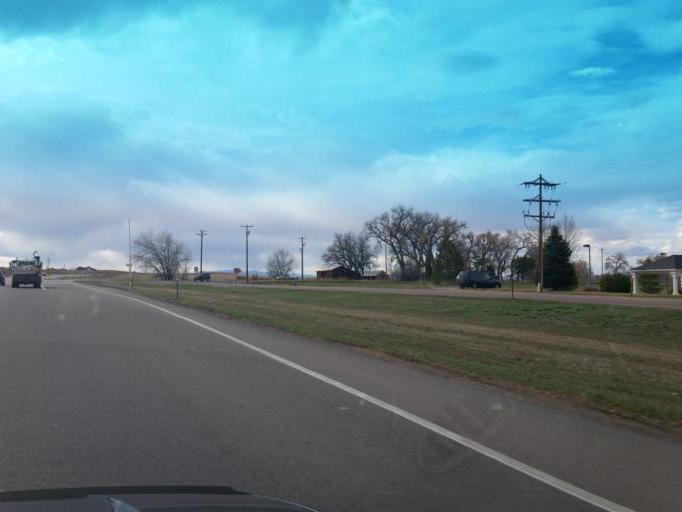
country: US
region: Colorado
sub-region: Weld County
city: Milliken
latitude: 40.3922
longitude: -104.7924
